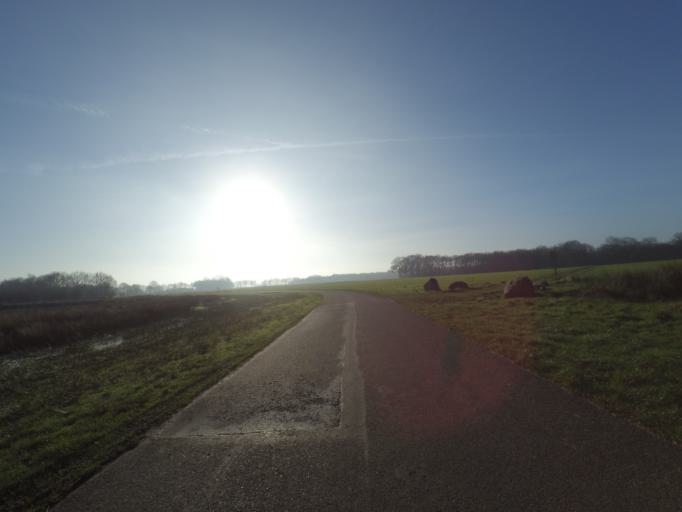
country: NL
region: Drenthe
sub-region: Gemeente Borger-Odoorn
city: Borger
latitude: 52.8464
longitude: 6.6495
